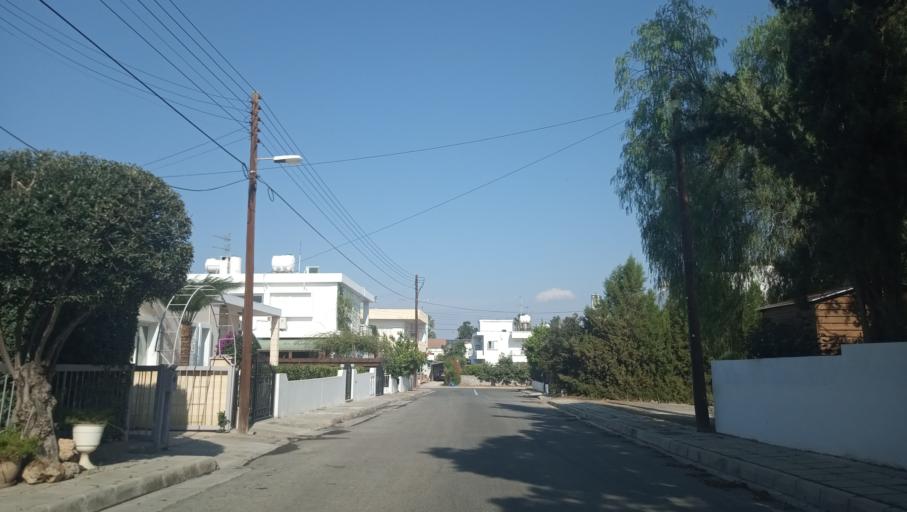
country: CY
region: Lefkosia
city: Nicosia
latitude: 35.1413
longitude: 33.3775
